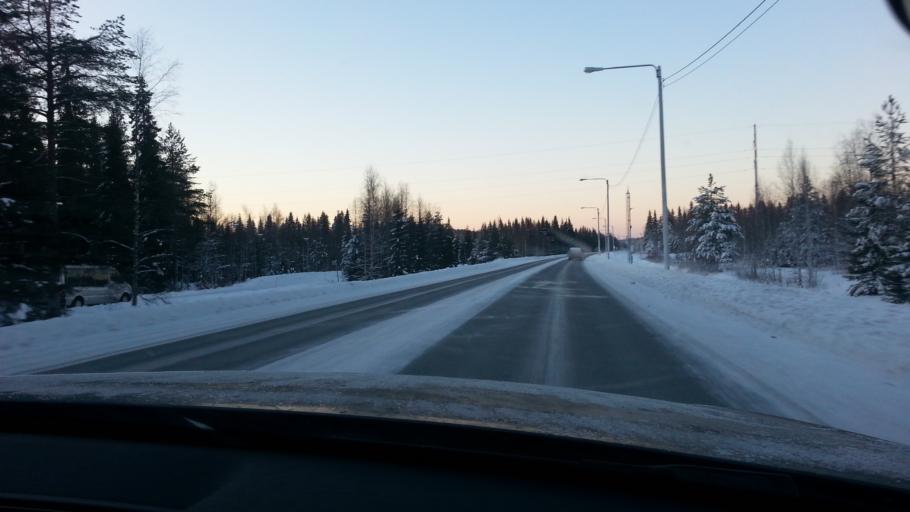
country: FI
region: Lapland
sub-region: Rovaniemi
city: Rovaniemi
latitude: 66.5432
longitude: 25.8356
